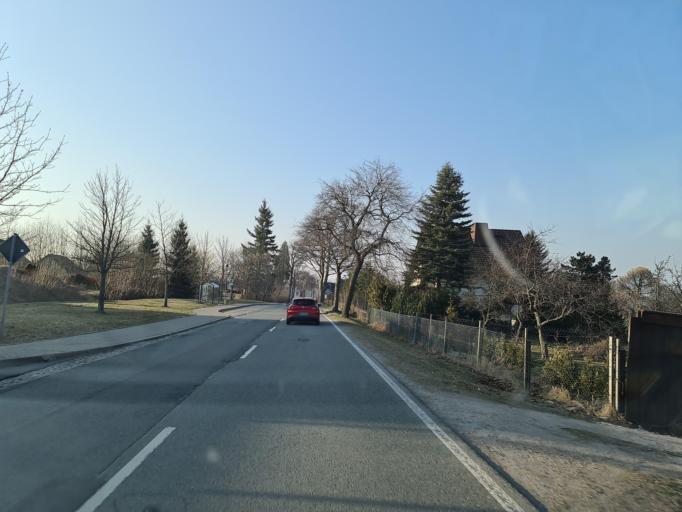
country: DE
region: Saxony
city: Eibenstock
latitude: 50.4891
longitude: 12.6075
